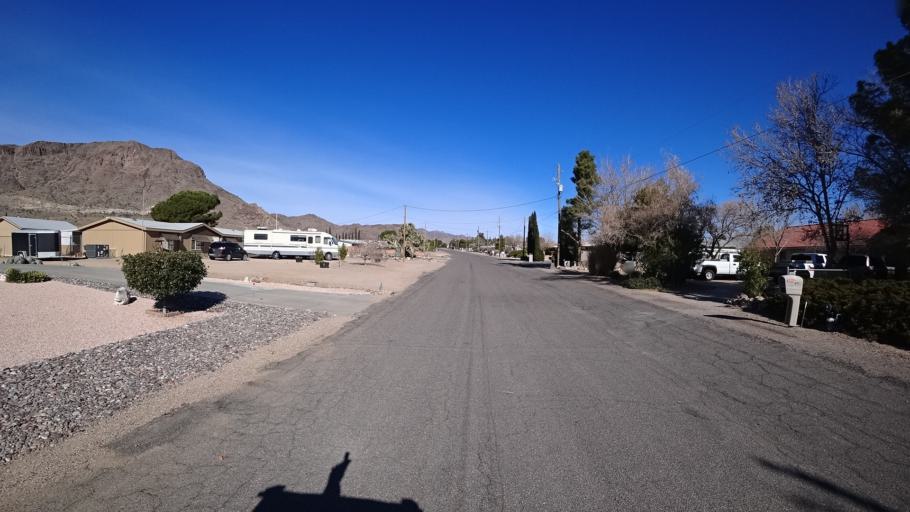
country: US
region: Arizona
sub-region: Mohave County
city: New Kingman-Butler
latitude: 35.2683
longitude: -114.0466
